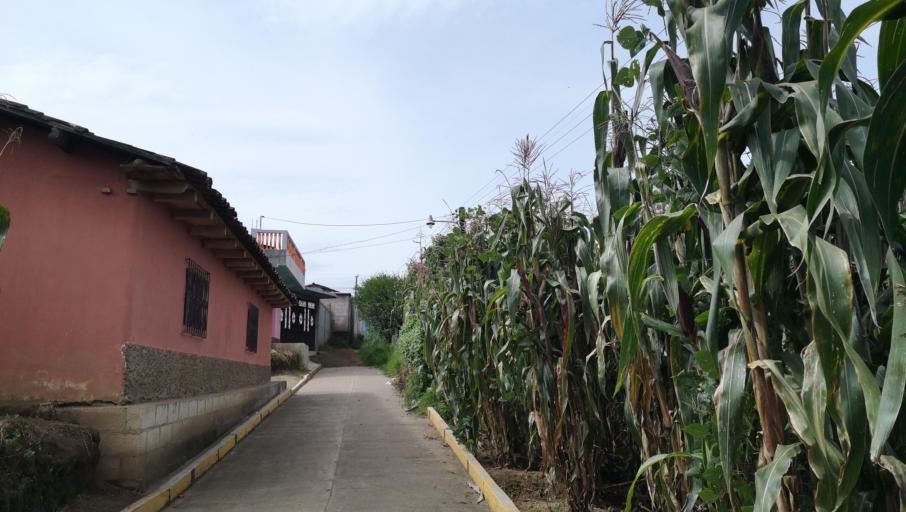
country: GT
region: Quetzaltenango
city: Cantel
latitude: 14.8192
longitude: -91.4419
